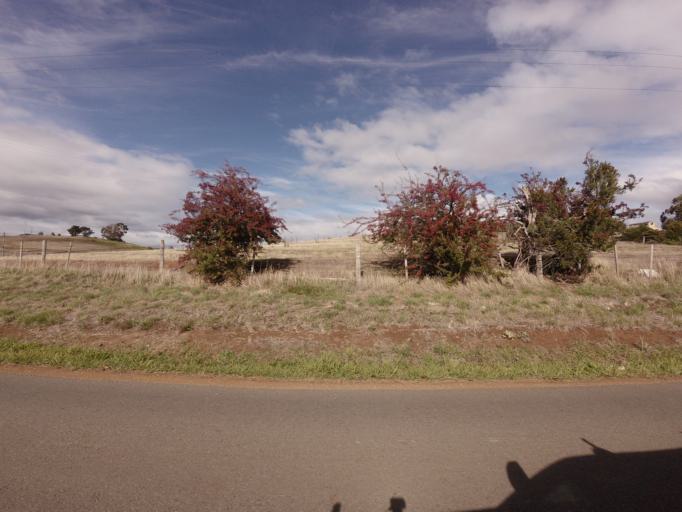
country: AU
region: Tasmania
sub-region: Derwent Valley
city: New Norfolk
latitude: -42.6982
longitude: 146.9204
